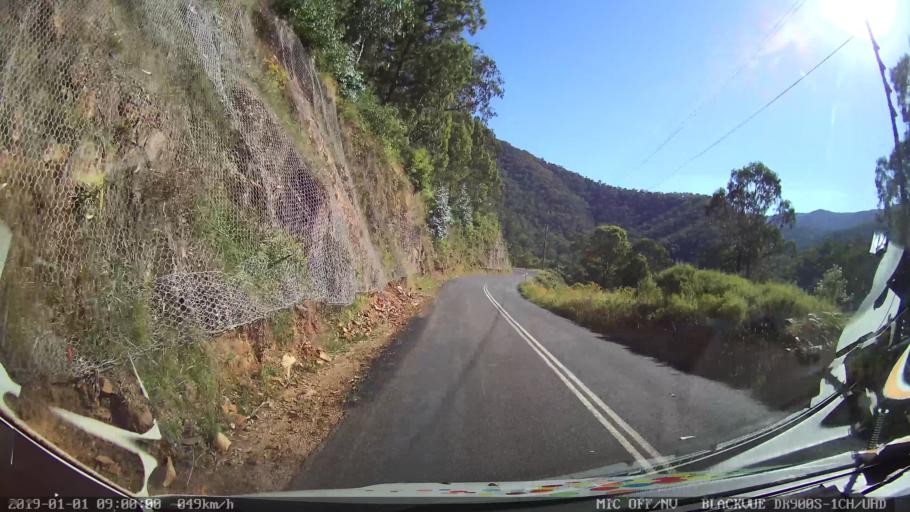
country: AU
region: New South Wales
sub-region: Snowy River
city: Jindabyne
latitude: -36.2378
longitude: 148.1806
